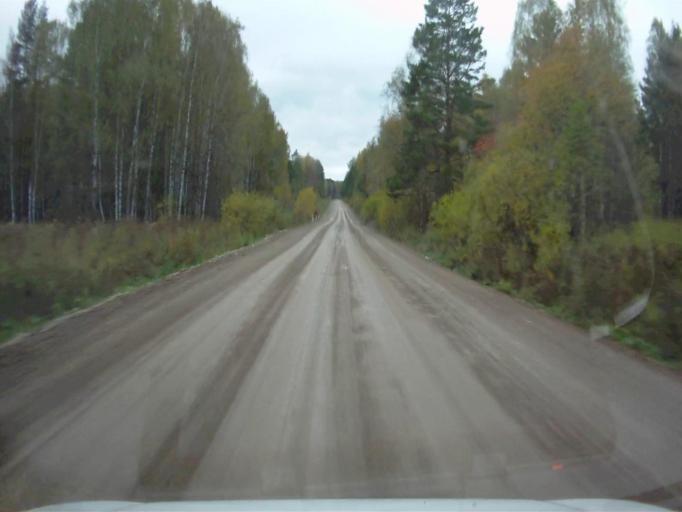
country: RU
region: Chelyabinsk
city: Nyazepetrovsk
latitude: 56.0935
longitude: 59.4068
